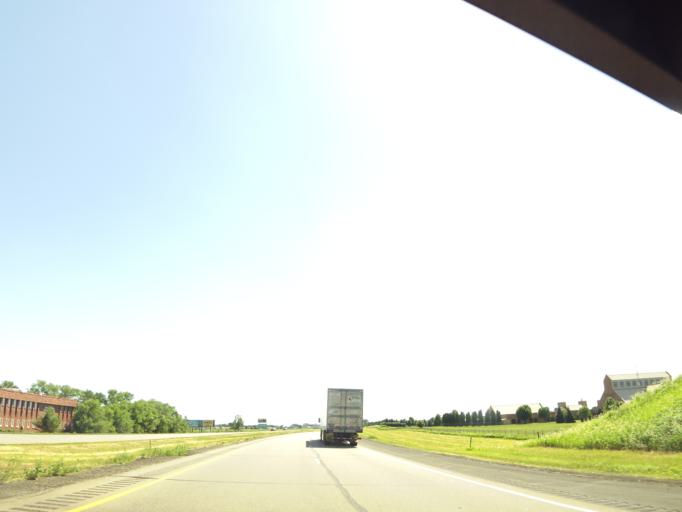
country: US
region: Minnesota
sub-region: Stearns County
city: Waite Park
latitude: 45.5405
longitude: -94.2076
